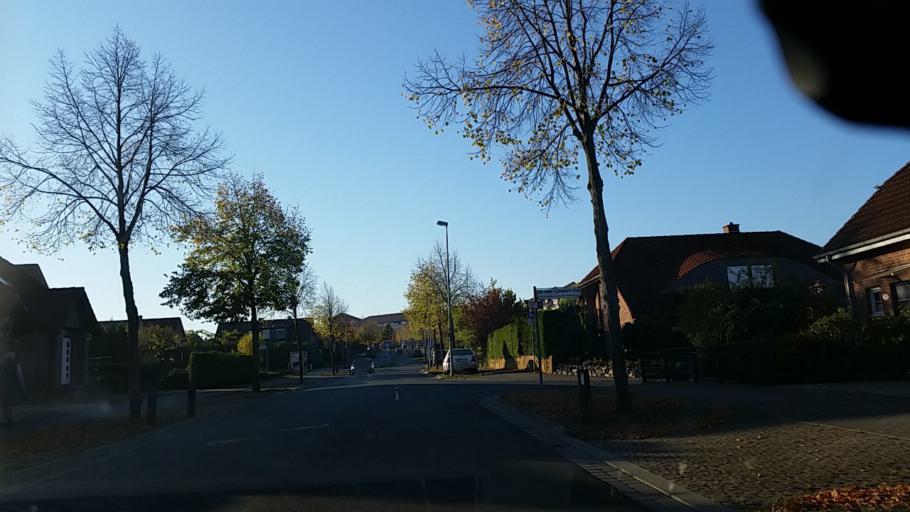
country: DE
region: Lower Saxony
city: Wolfsburg
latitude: 52.4183
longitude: 10.8318
